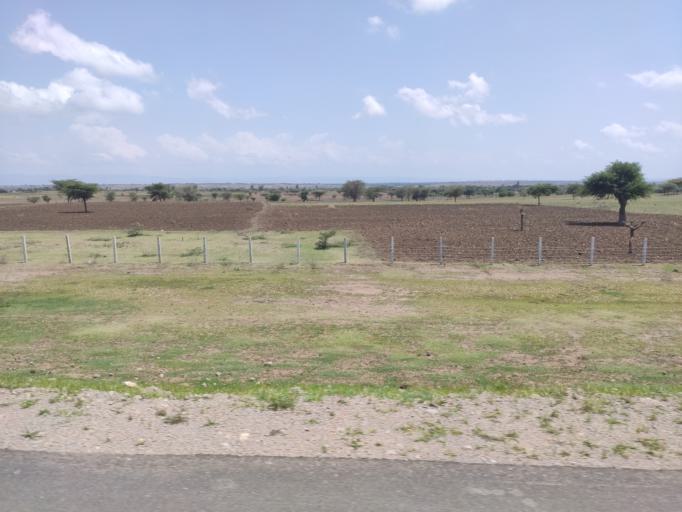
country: ET
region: Oromiya
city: Ziway
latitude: 8.2667
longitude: 38.9047
